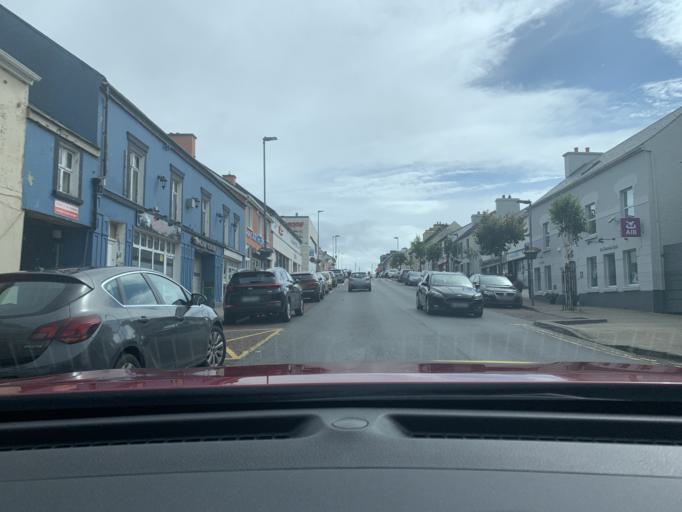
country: IE
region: Ulster
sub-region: County Donegal
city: Dungloe
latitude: 54.9494
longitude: -8.3604
